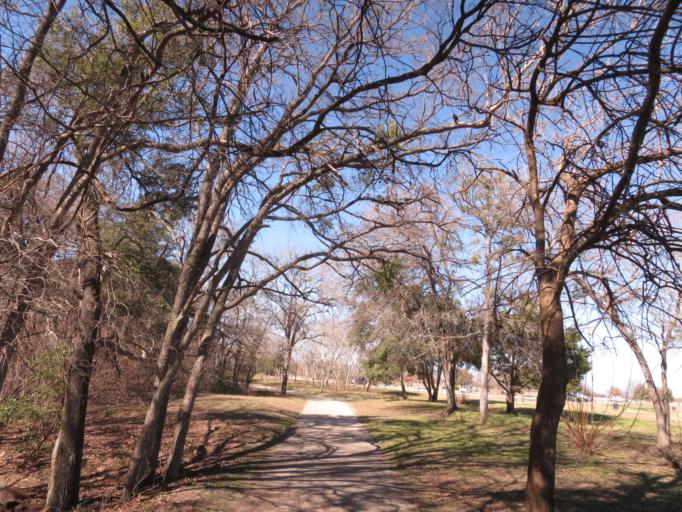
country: US
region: Texas
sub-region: Williamson County
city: Round Rock
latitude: 30.5303
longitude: -97.6316
